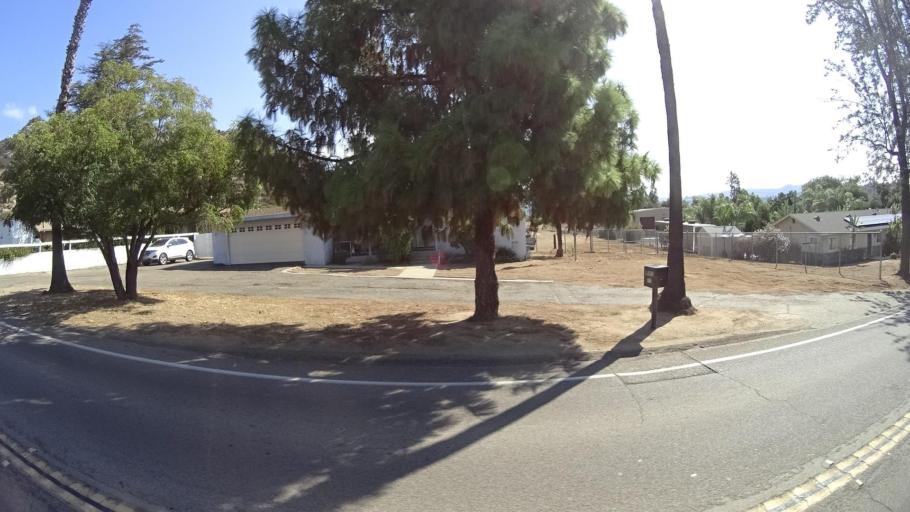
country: US
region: California
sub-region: San Diego County
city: Eucalyptus Hills
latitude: 32.8627
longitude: -116.9551
